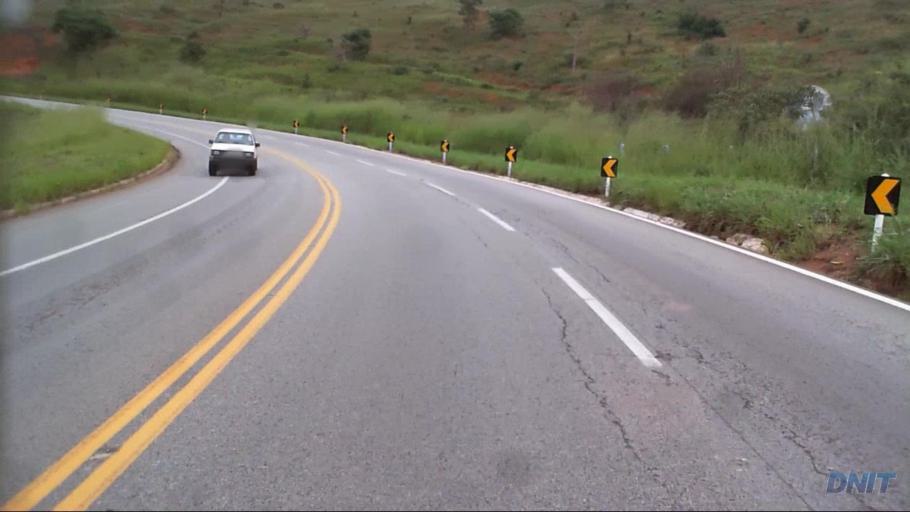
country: BR
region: Minas Gerais
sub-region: Nova Era
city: Nova Era
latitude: -19.7940
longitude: -43.0557
